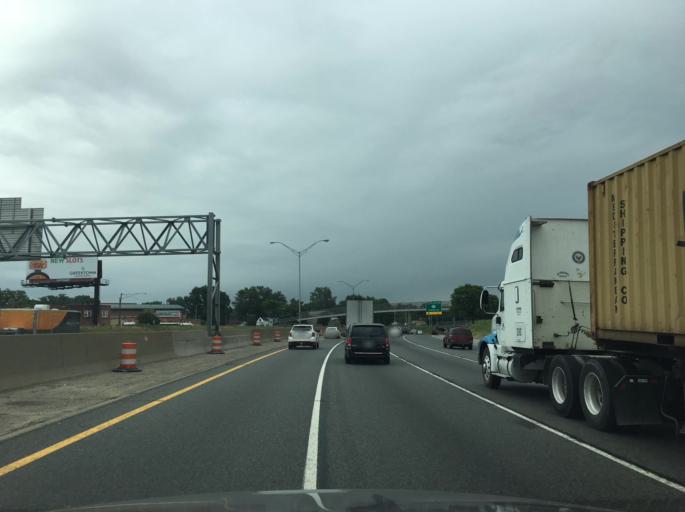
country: US
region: Michigan
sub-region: Oakland County
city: Hazel Park
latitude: 42.4575
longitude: -83.0984
